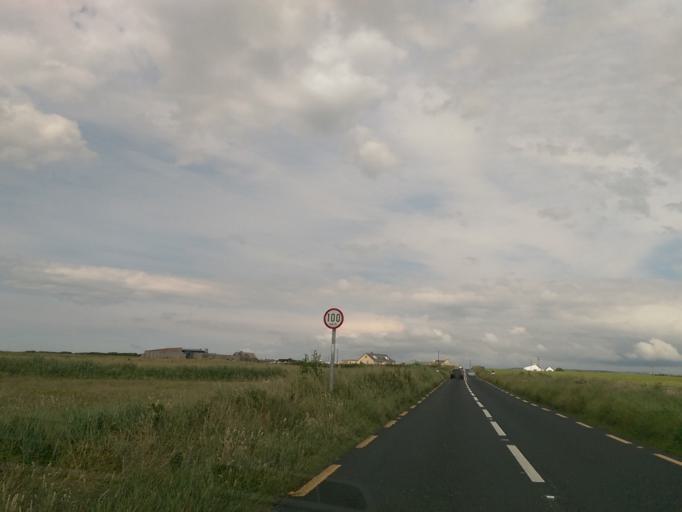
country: IE
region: Munster
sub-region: An Clar
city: Kilrush
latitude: 52.8200
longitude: -9.4519
